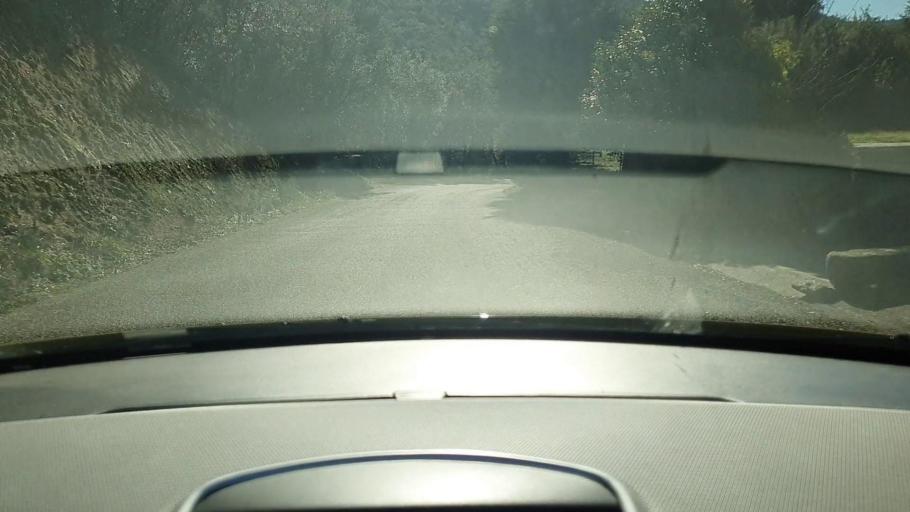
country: FR
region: Languedoc-Roussillon
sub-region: Departement du Gard
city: Valleraugue
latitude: 44.0489
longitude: 3.6925
